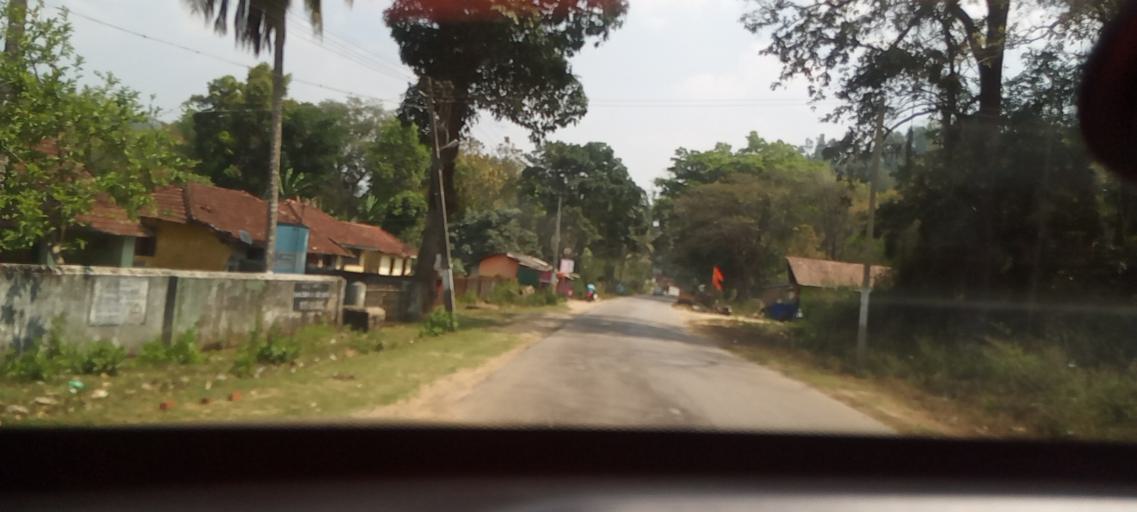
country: IN
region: Karnataka
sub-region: Chikmagalur
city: Chikmagalur
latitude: 13.3390
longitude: 75.5469
